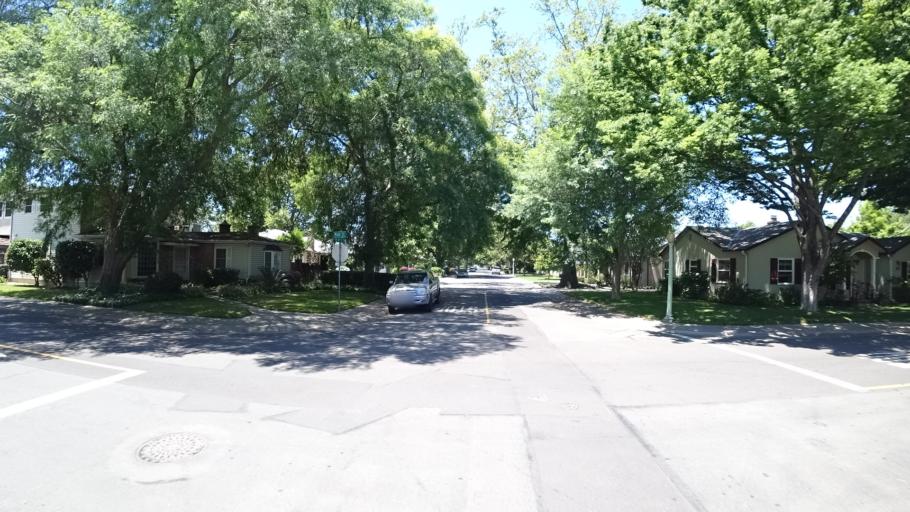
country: US
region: California
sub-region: Sacramento County
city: Sacramento
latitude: 38.5558
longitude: -121.5073
